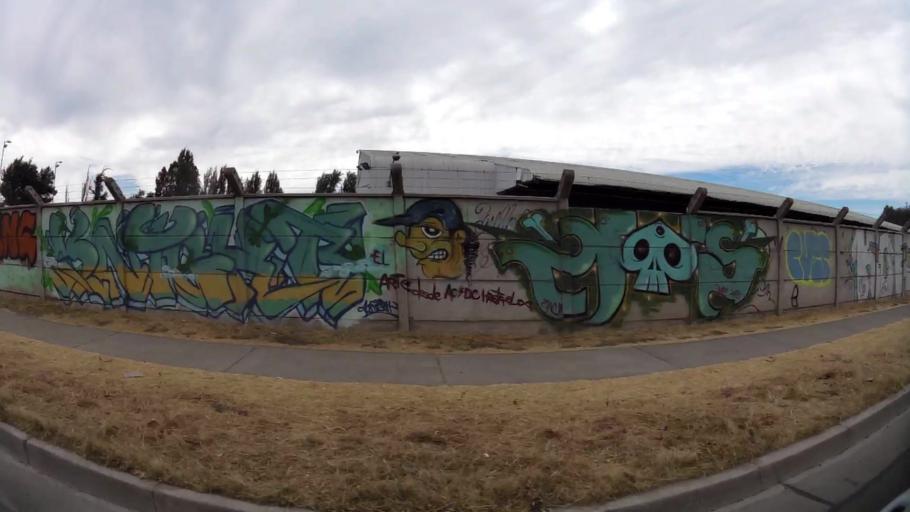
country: CL
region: O'Higgins
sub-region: Provincia de Cachapoal
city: Rancagua
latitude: -34.1387
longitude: -70.7428
